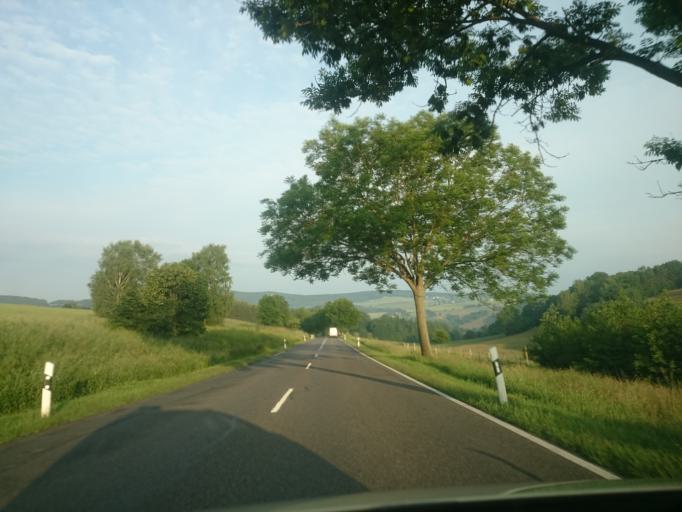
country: DE
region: Saxony
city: Pockau
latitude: 50.7104
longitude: 13.2448
